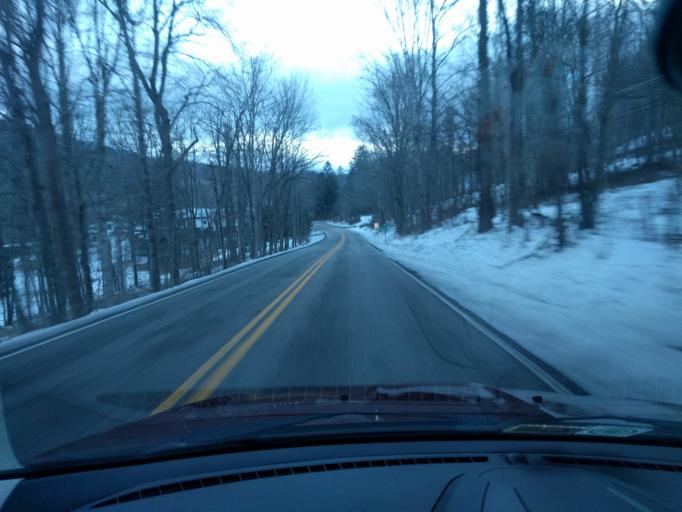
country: US
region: Virginia
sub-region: Bath County
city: Warm Springs
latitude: 37.9604
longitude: -79.8631
